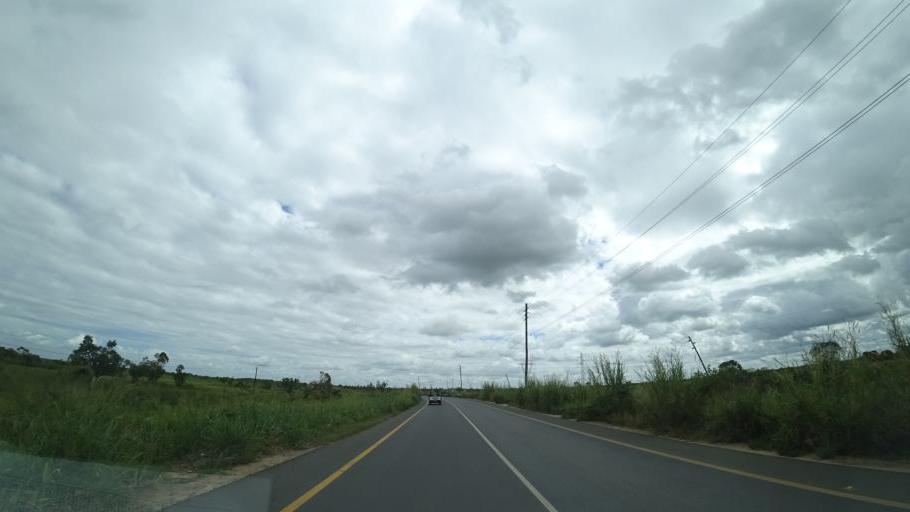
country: MZ
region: Sofala
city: Dondo
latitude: -19.5169
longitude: 34.6196
